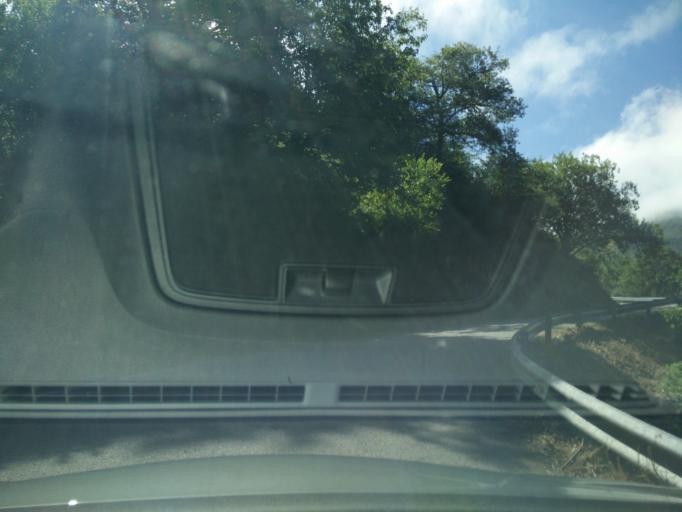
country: ES
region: Asturias
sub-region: Province of Asturias
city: Pola de Somiedo
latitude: 43.0814
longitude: -6.2291
